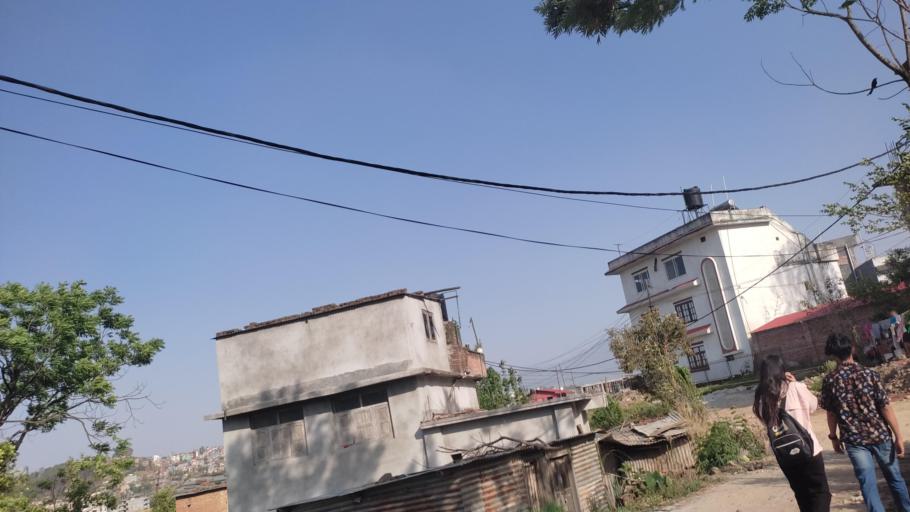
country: NP
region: Central Region
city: Kirtipur
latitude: 27.6533
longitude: 85.2805
